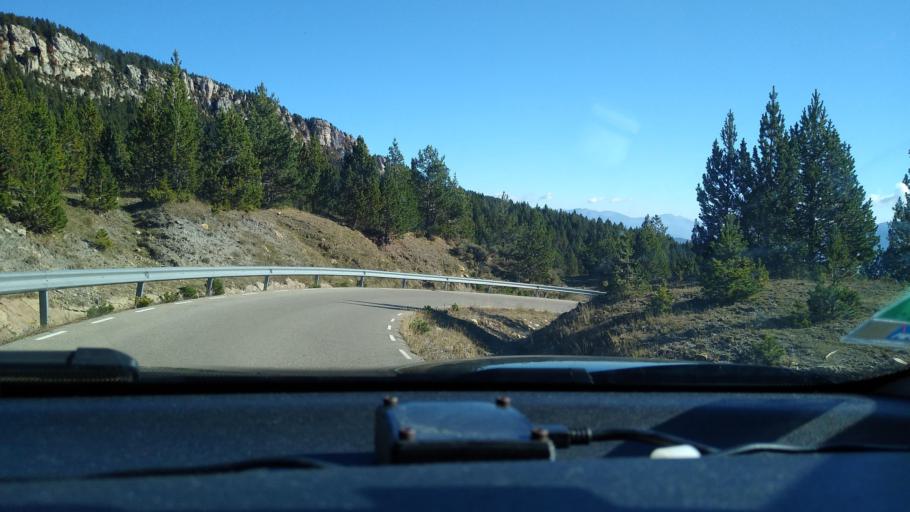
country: ES
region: Catalonia
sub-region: Provincia de Barcelona
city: Vallcebre
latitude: 42.2018
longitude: 1.7725
